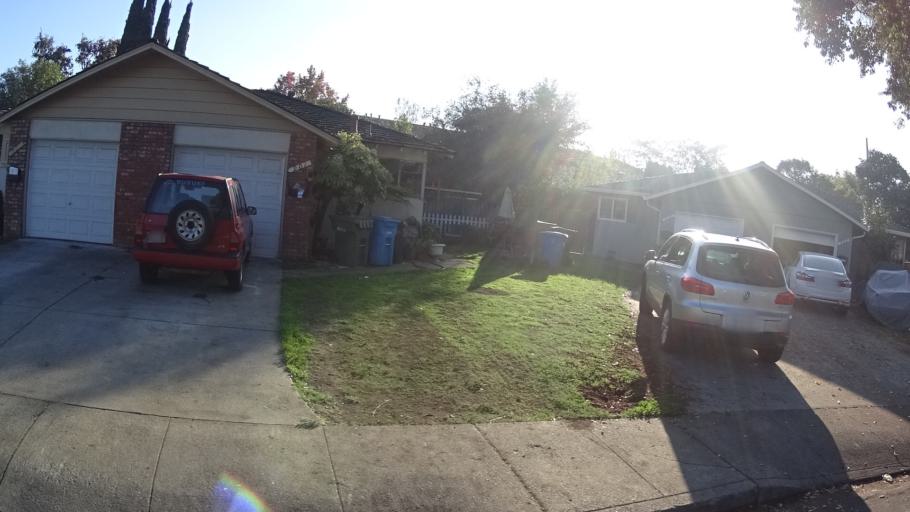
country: US
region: California
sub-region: Santa Clara County
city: Santa Clara
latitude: 37.3415
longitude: -121.9853
